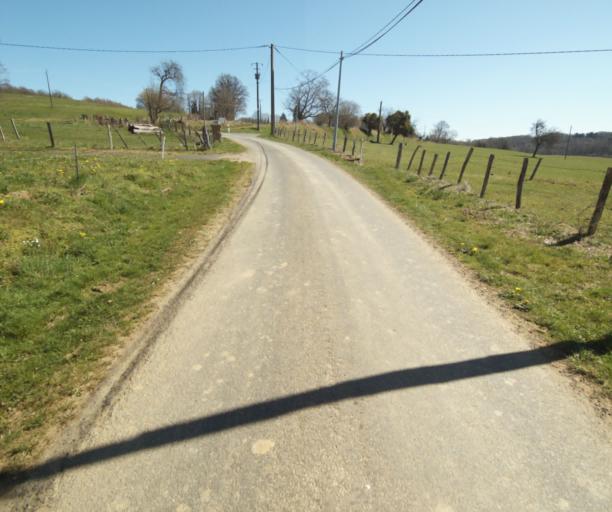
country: FR
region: Limousin
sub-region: Departement de la Correze
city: Chamboulive
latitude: 45.3967
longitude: 1.6530
